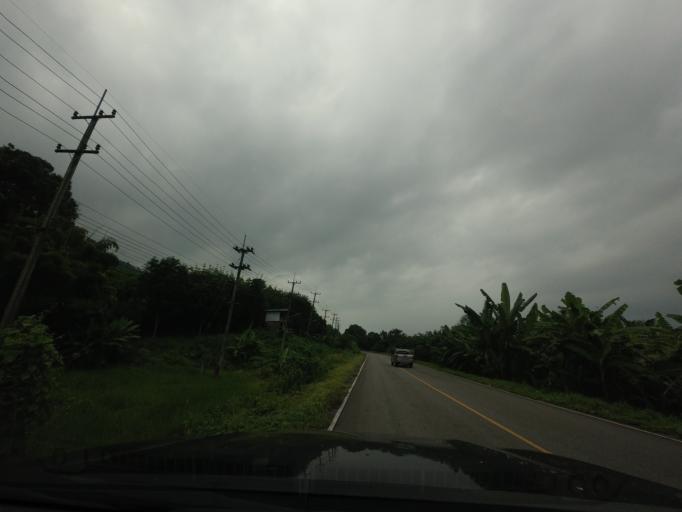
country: TH
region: Nong Khai
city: Sangkhom
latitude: 18.0455
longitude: 102.3301
